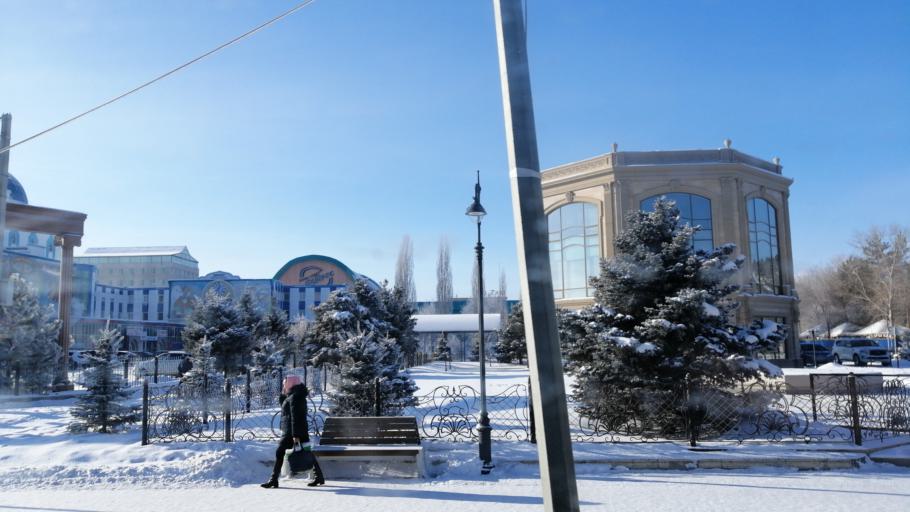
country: KZ
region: Aqtoebe
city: Aqtobe
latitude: 50.2973
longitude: 57.1566
